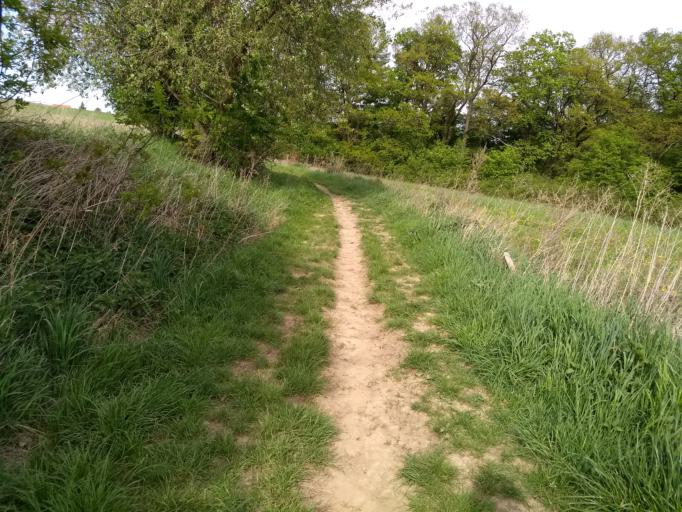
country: CZ
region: Central Bohemia
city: Unhost'
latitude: 50.0466
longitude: 14.1650
